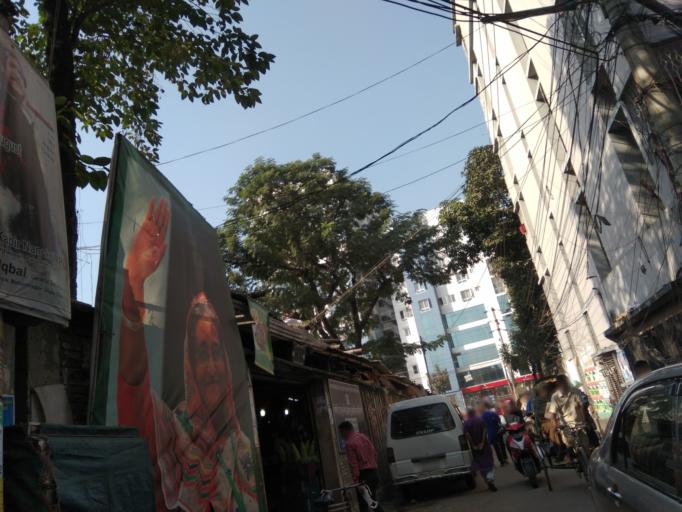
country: BD
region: Dhaka
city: Azimpur
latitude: 23.7739
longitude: 90.3642
